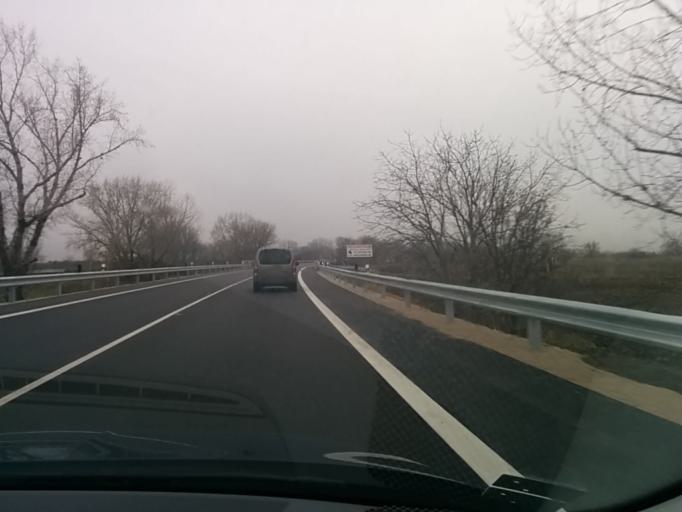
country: SK
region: Trnavsky
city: Sladkovicovo
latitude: 48.1949
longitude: 17.6080
